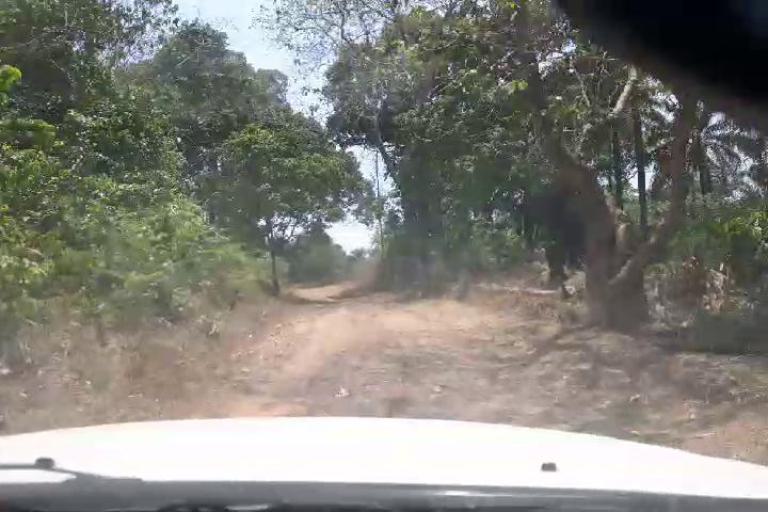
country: SL
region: Northern Province
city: Alikalia
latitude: 9.0719
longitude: -11.4830
